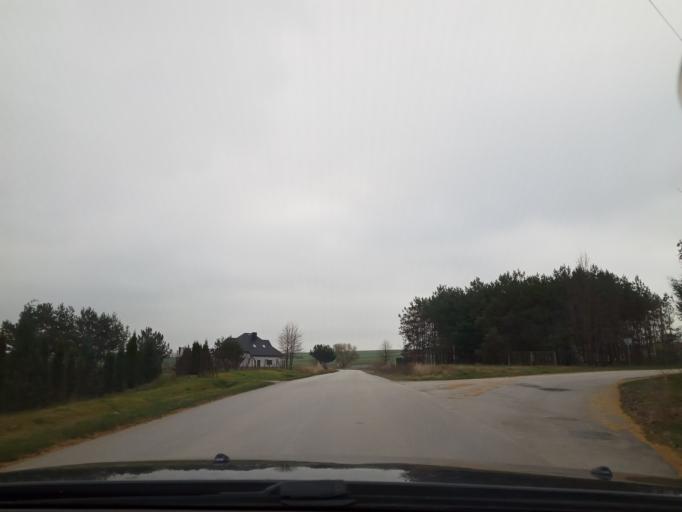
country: PL
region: Swietokrzyskie
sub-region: Powiat jedrzejowski
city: Imielno
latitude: 50.5922
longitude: 20.4242
